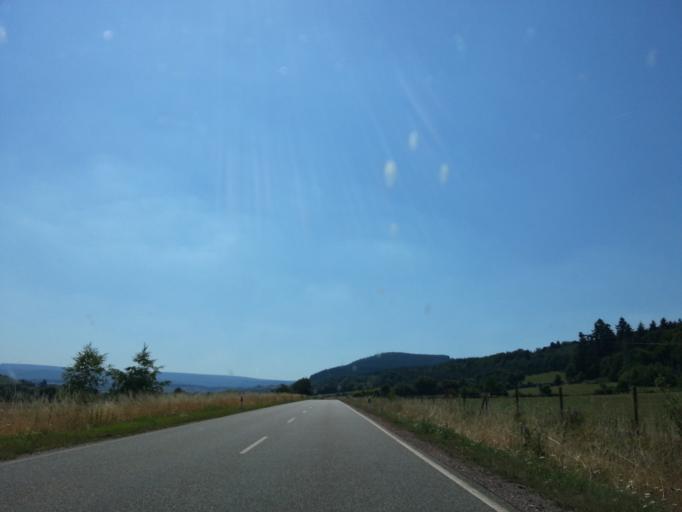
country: DE
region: Rheinland-Pfalz
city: Altrich
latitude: 49.9364
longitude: 6.9325
